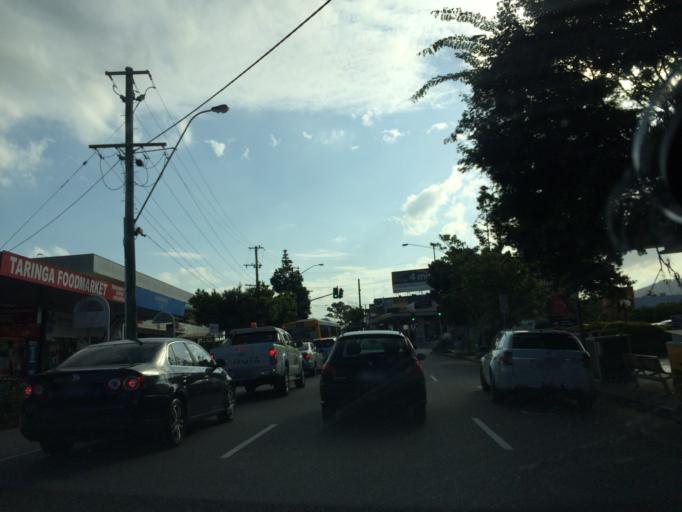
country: AU
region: Queensland
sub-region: Brisbane
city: Taringa
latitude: -27.4928
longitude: 152.9794
